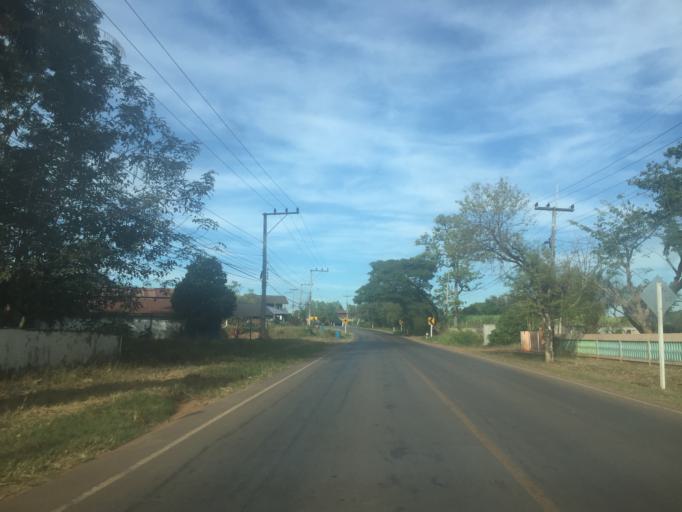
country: TH
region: Changwat Udon Thani
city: Si That
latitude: 16.9897
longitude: 103.1723
